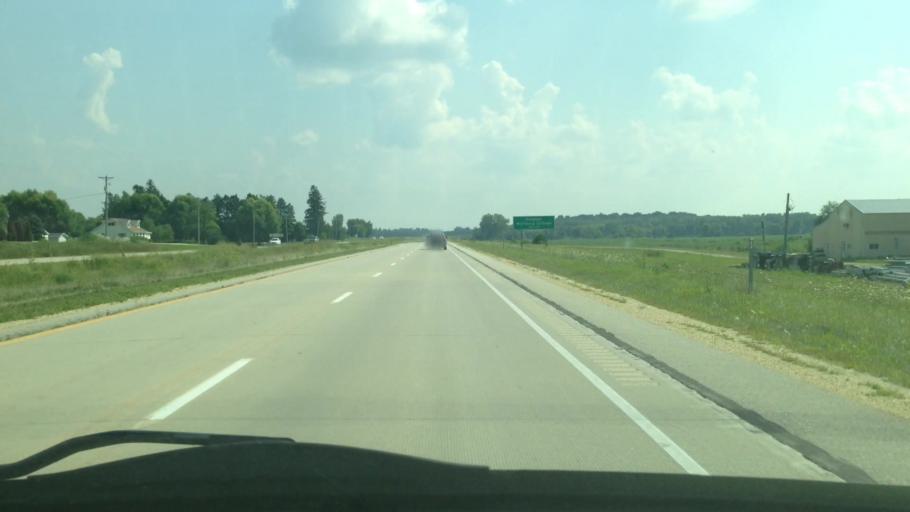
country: US
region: Iowa
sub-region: Bremer County
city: Denver
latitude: 42.7292
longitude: -92.3382
